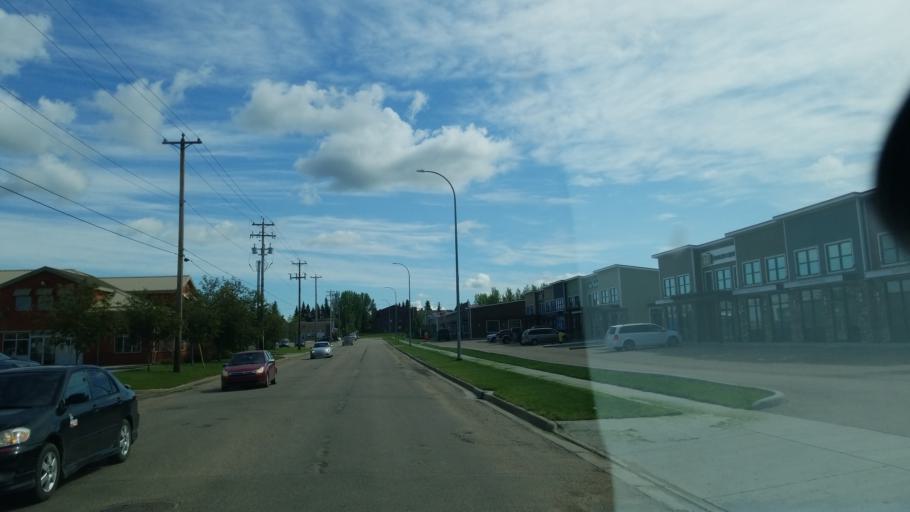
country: CA
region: Saskatchewan
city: Lloydminster
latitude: 53.2731
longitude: -110.0086
